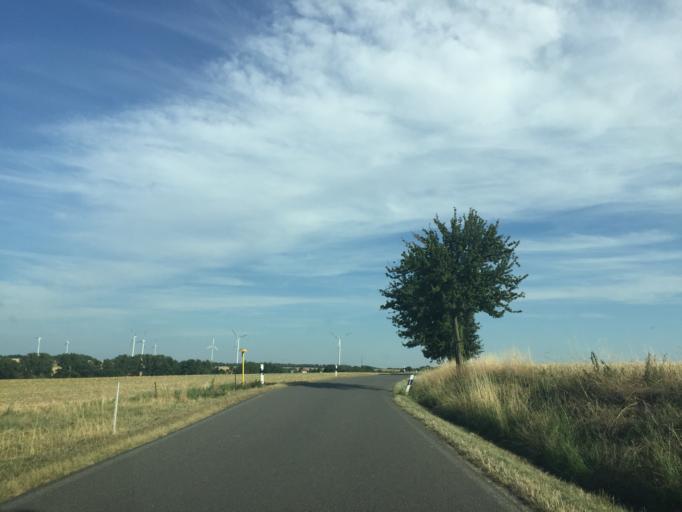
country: DE
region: Thuringia
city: Schmolln
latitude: 50.8829
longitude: 12.3686
